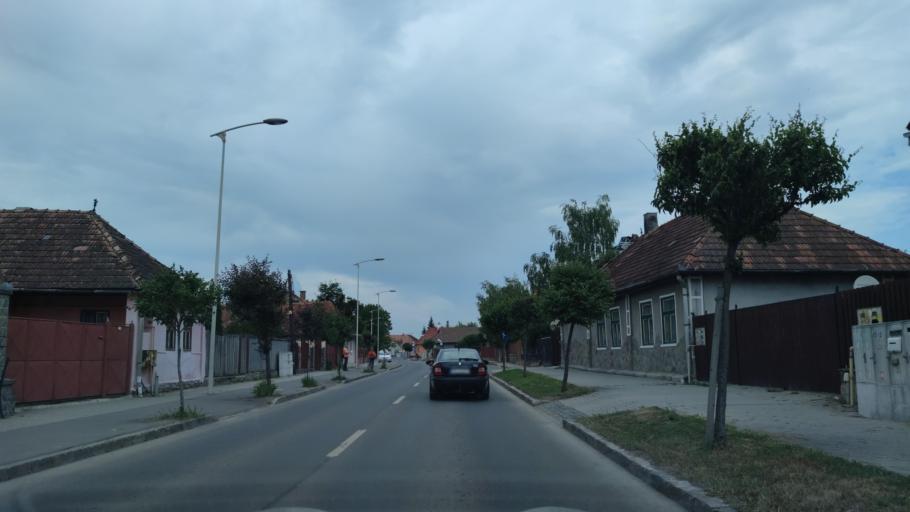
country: RO
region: Harghita
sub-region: Municipiul Miercurea Ciuc
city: Miercurea-Ciuc
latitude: 46.3746
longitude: 25.8022
